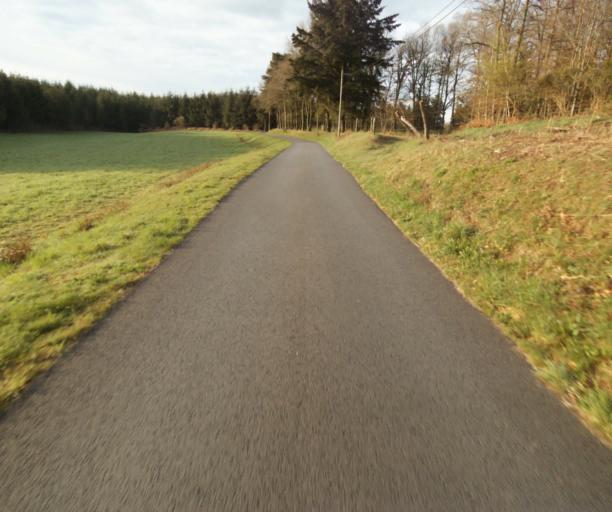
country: FR
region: Limousin
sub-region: Departement de la Correze
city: Correze
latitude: 45.4057
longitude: 1.8731
